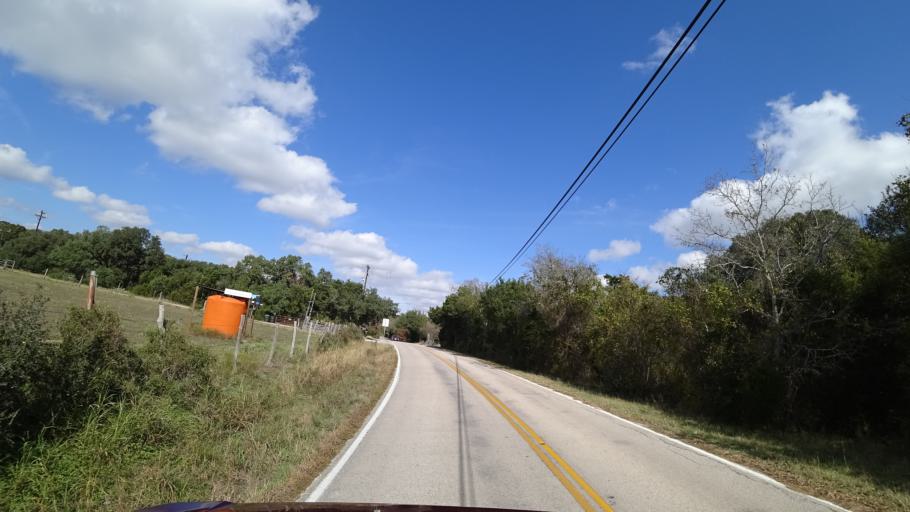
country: US
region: Texas
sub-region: Williamson County
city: Jollyville
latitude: 30.4188
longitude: -97.7941
